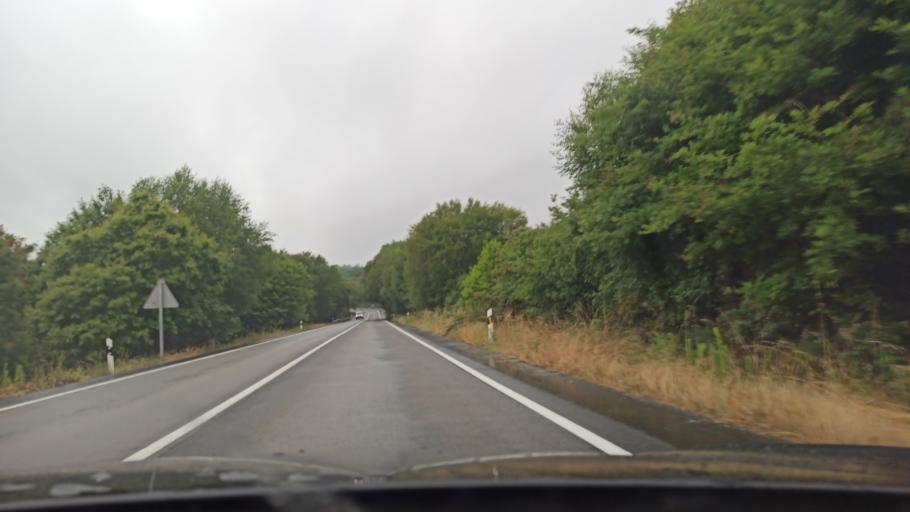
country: ES
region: Galicia
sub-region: Provincia de Lugo
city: Guntin
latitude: 42.8376
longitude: -7.7531
